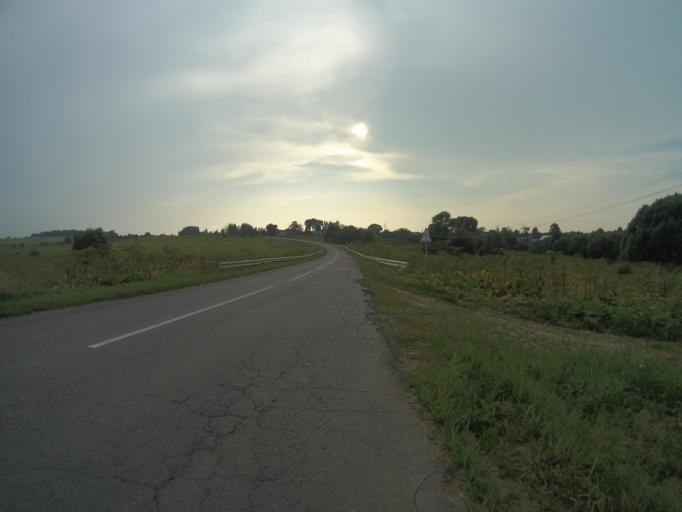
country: RU
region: Ivanovo
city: Gavrilov Posad
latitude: 56.3468
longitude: 40.1545
